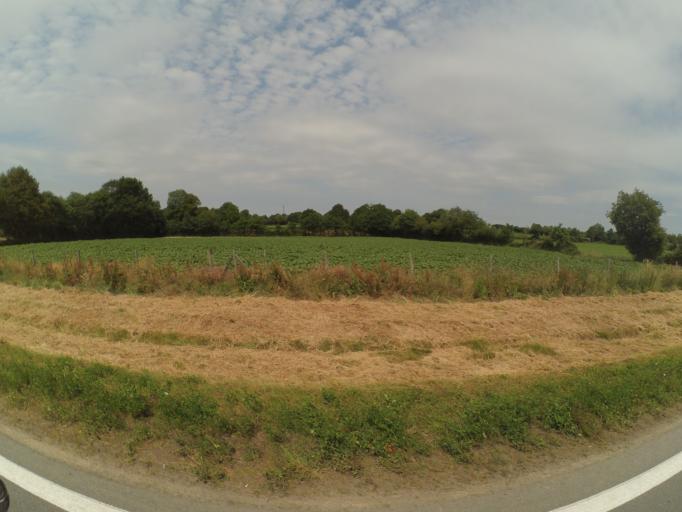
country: FR
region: Pays de la Loire
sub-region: Departement de la Vendee
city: Saint-Paul-en-Pareds
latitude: 46.8612
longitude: -0.9737
